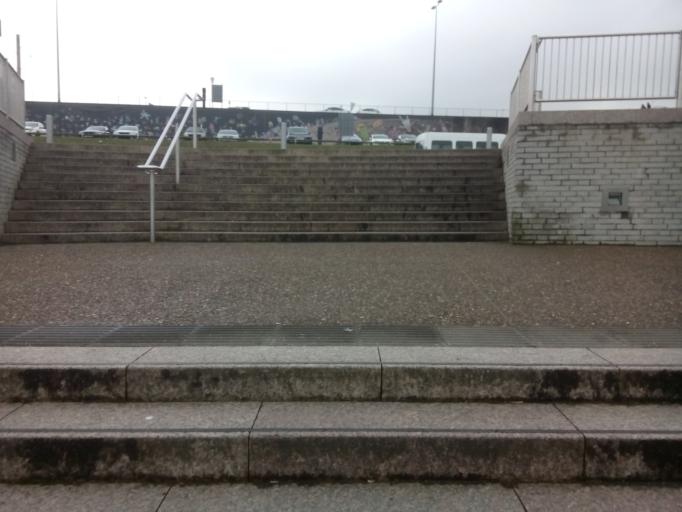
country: GB
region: England
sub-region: Gateshead
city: Gateshead
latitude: 54.9690
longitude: -1.5994
